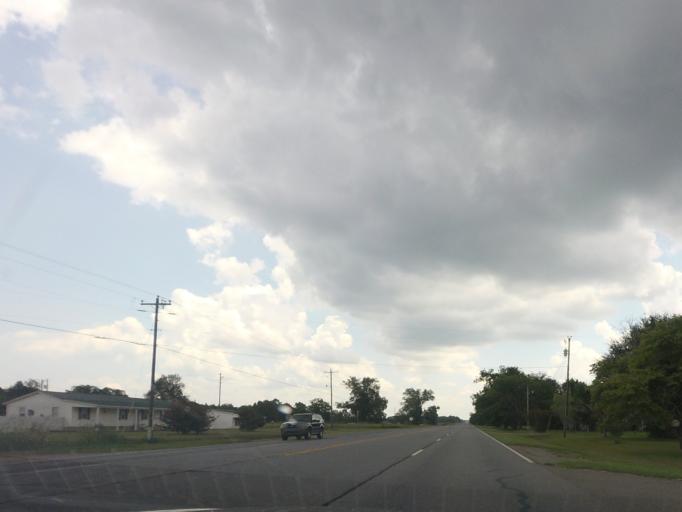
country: US
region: Georgia
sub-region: Bleckley County
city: Cochran
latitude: 32.4315
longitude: -83.3704
